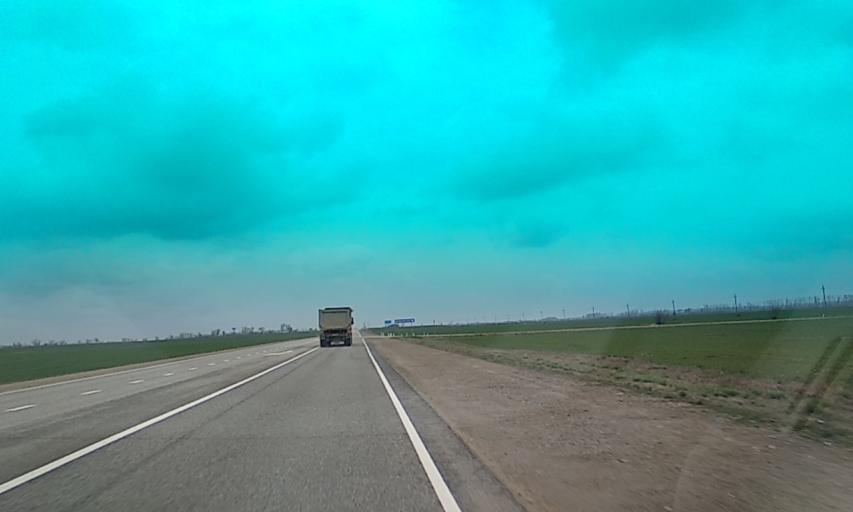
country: RU
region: Krasnodarskiy
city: Velikovechnoye
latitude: 44.9136
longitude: 39.7943
